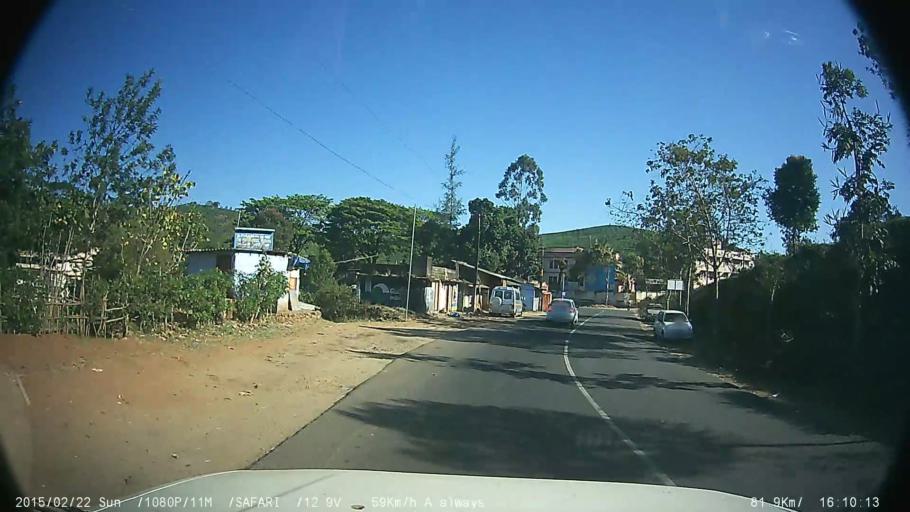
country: IN
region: Tamil Nadu
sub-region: Theni
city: Gudalur
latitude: 9.5703
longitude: 77.0856
